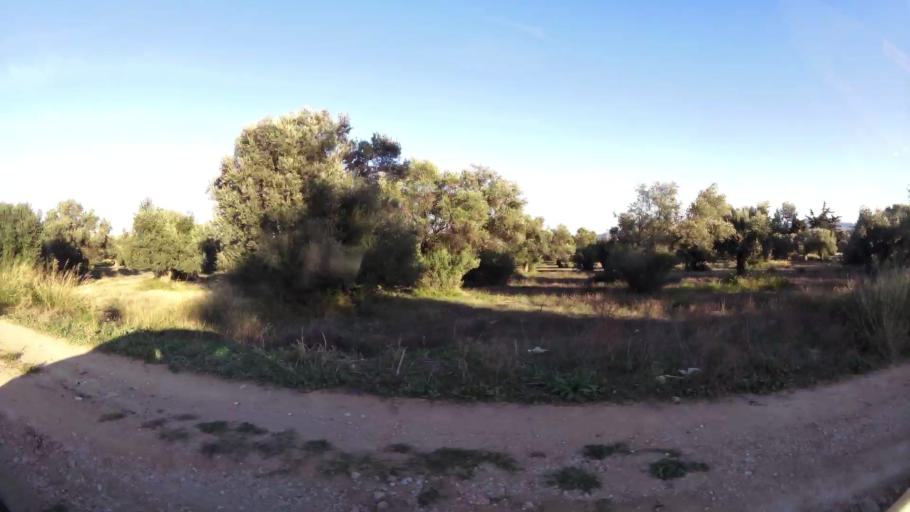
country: GR
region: Attica
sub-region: Nomarchia Anatolikis Attikis
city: Spata
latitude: 37.9575
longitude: 23.9230
